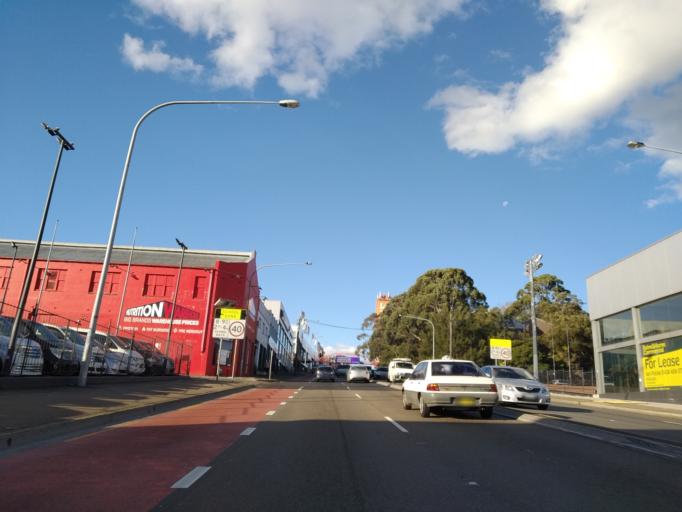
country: AU
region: New South Wales
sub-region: Marrickville
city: Lewisham
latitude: -33.8895
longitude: 151.1506
